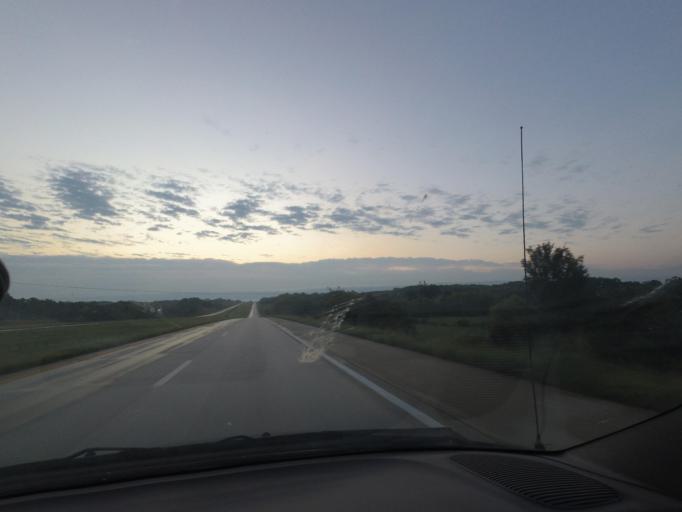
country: US
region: Missouri
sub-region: Macon County
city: Macon
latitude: 39.7591
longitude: -92.6635
